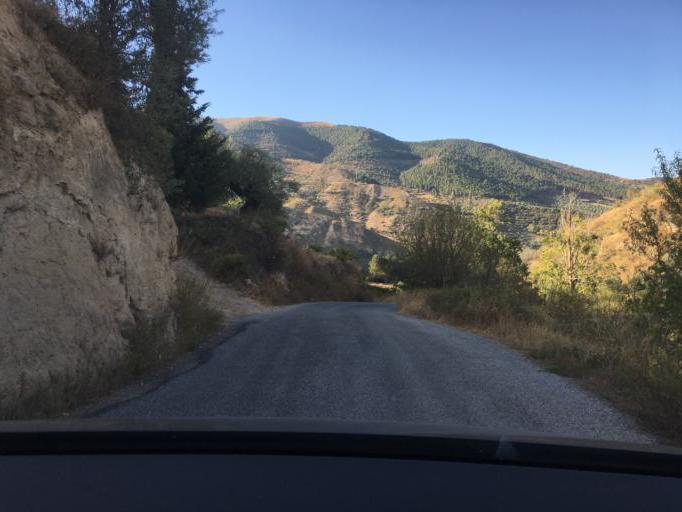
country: ES
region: Andalusia
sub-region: Provincia de Granada
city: Quentar
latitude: 37.1976
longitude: -3.4645
